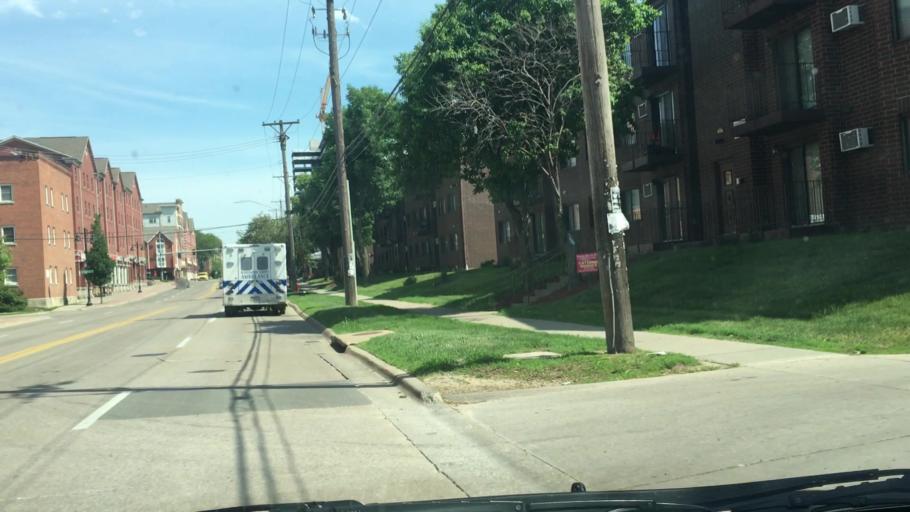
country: US
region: Iowa
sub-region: Johnson County
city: Iowa City
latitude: 41.6560
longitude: -91.5301
